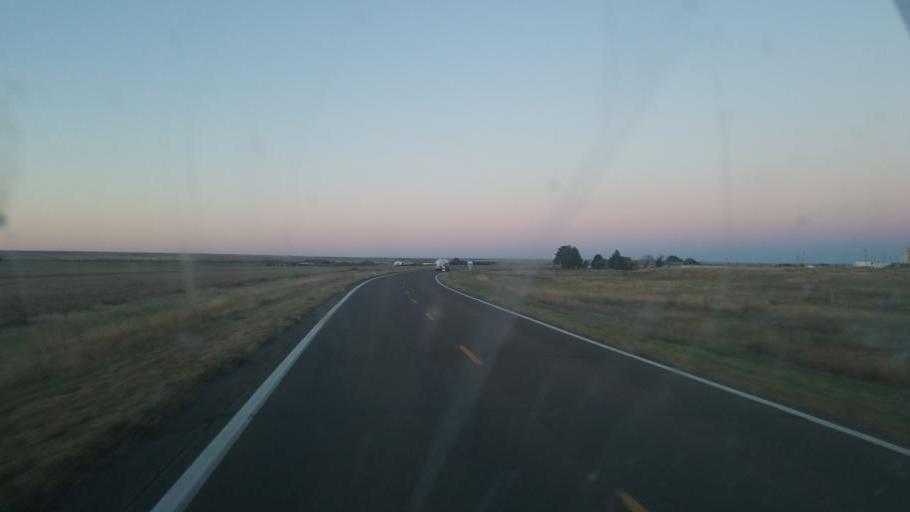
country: US
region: Kansas
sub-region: Wallace County
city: Sharon Springs
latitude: 38.9123
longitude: -101.5772
